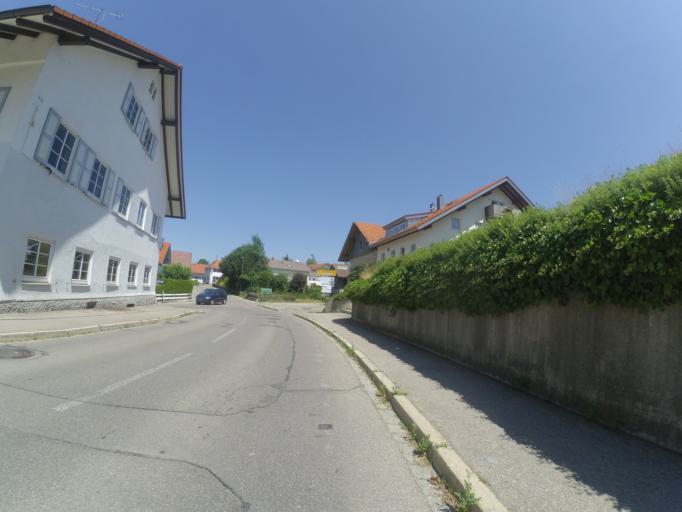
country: DE
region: Bavaria
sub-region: Swabia
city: Haldenwang
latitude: 47.8016
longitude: 10.3465
